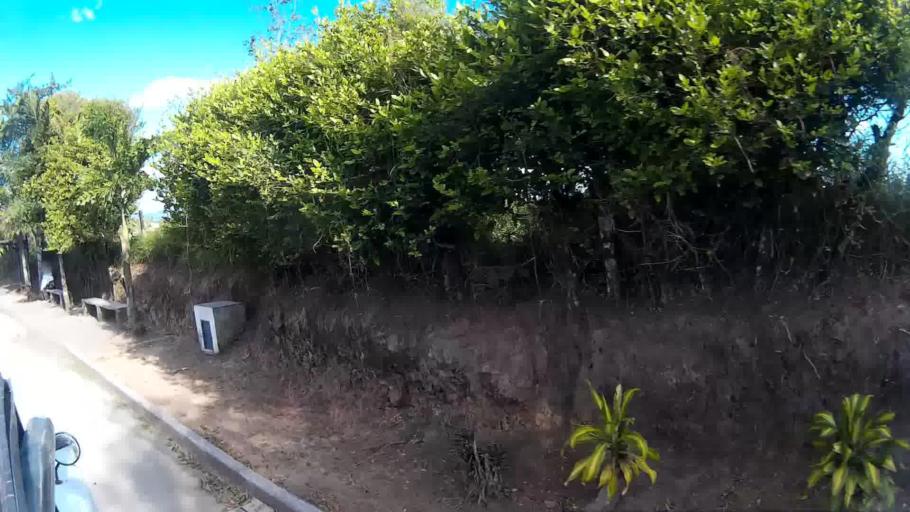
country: CO
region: Quindio
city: Filandia
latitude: 4.7194
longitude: -75.6810
